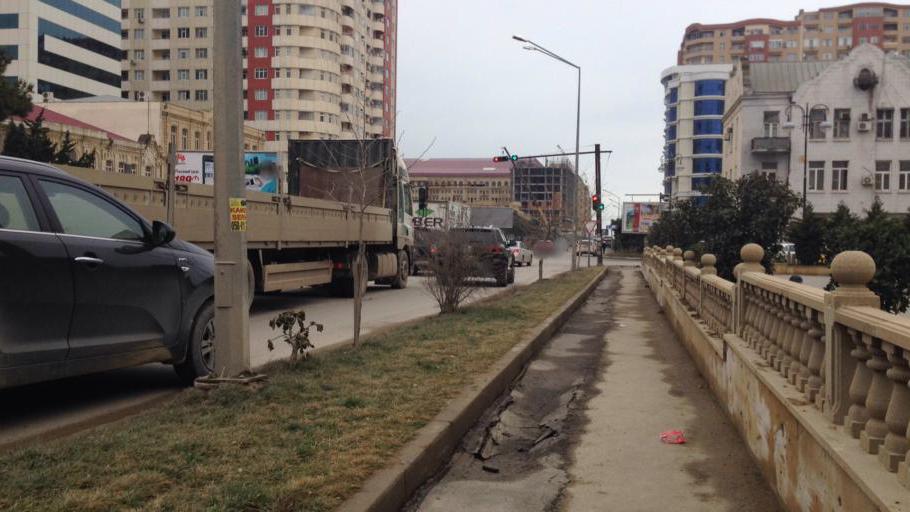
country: AZ
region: Baki
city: Baku
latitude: 40.3842
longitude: 49.8766
